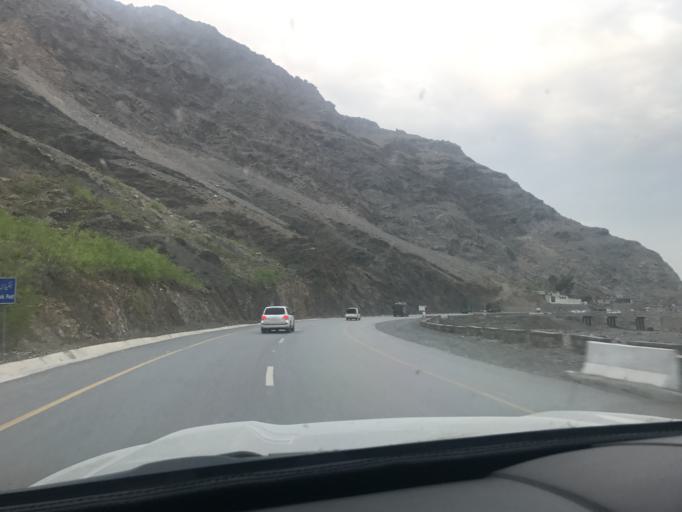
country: PK
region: Federally Administered Tribal Areas
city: Landi Kotal
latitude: 34.0066
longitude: 71.3137
